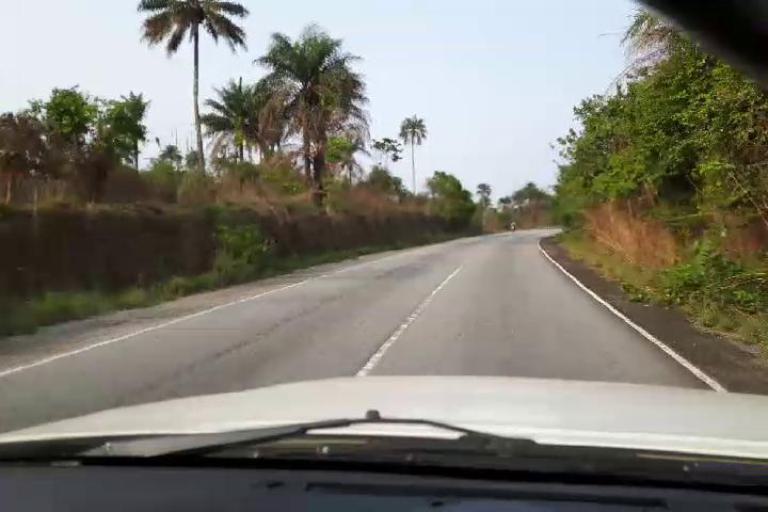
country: SL
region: Eastern Province
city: Blama
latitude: 7.9407
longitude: -11.5033
